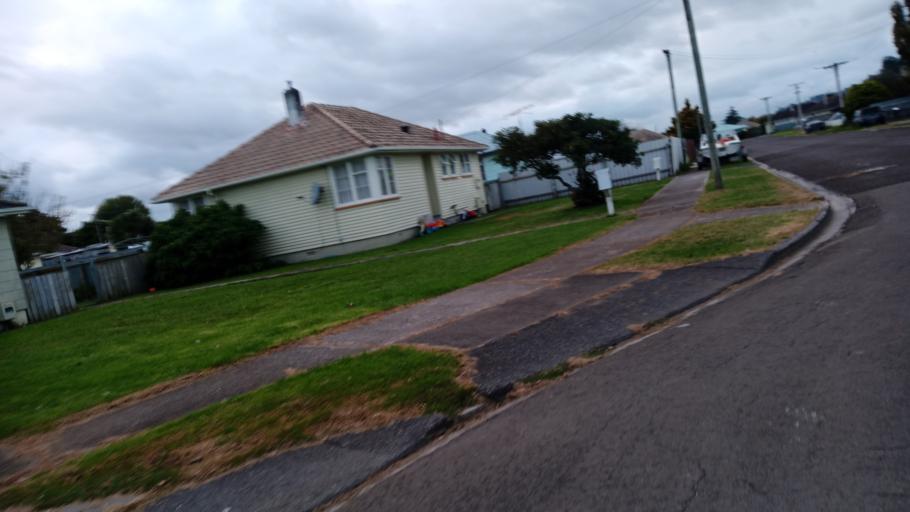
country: NZ
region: Gisborne
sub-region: Gisborne District
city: Gisborne
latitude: -38.6585
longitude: 177.9917
